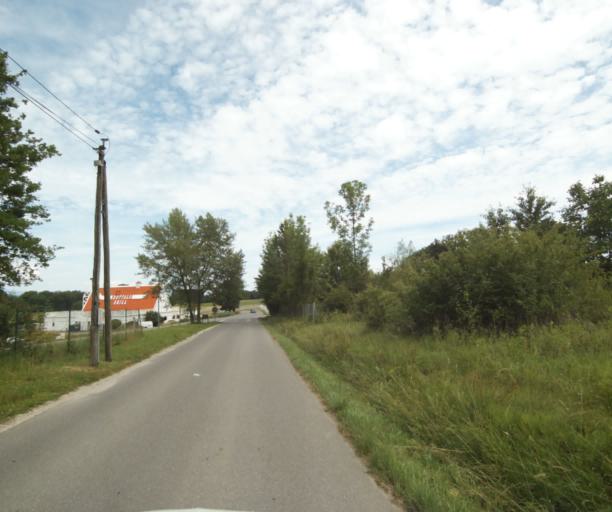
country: FR
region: Rhone-Alpes
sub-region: Departement de la Haute-Savoie
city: Anthy-sur-Leman
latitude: 46.3447
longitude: 6.4220
